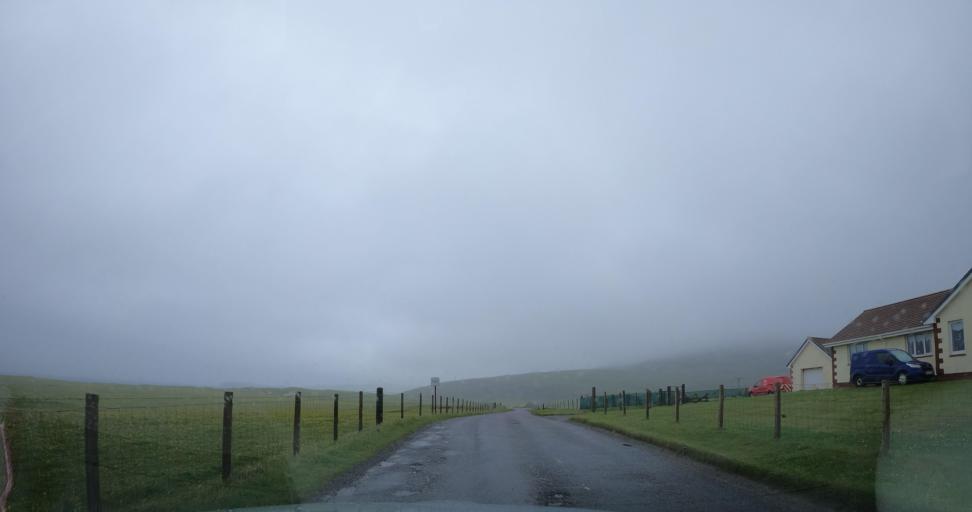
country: GB
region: Scotland
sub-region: Eilean Siar
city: Barra
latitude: 56.9823
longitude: -7.5109
